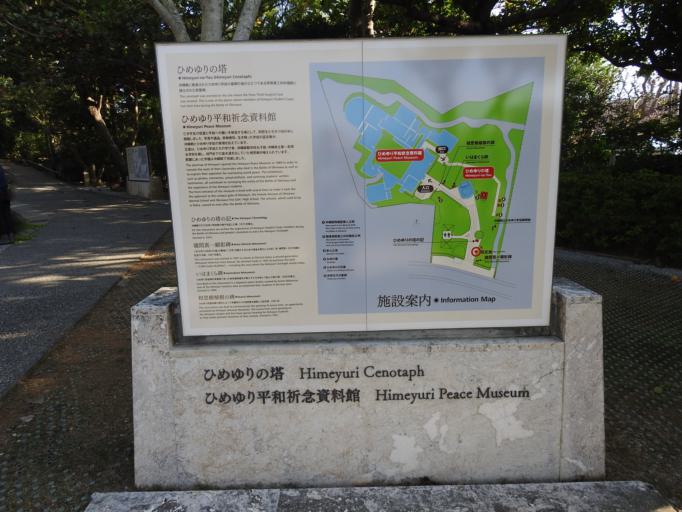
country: JP
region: Okinawa
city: Itoman
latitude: 26.0959
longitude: 127.6908
